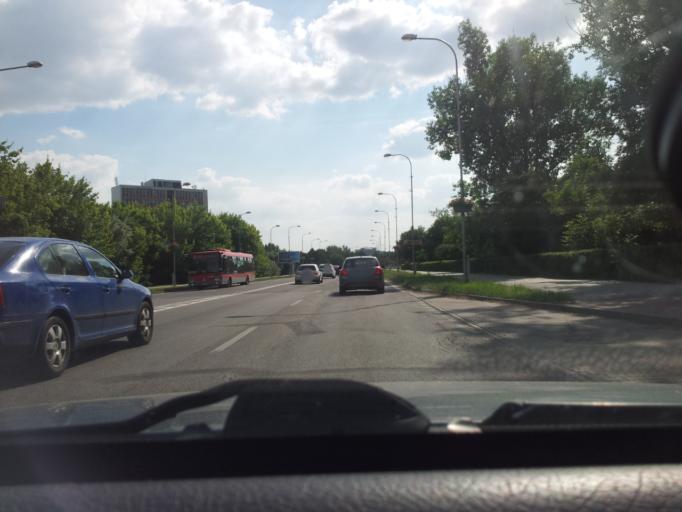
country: SK
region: Nitriansky
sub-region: Okres Nitra
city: Nitra
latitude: 48.3092
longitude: 18.0954
